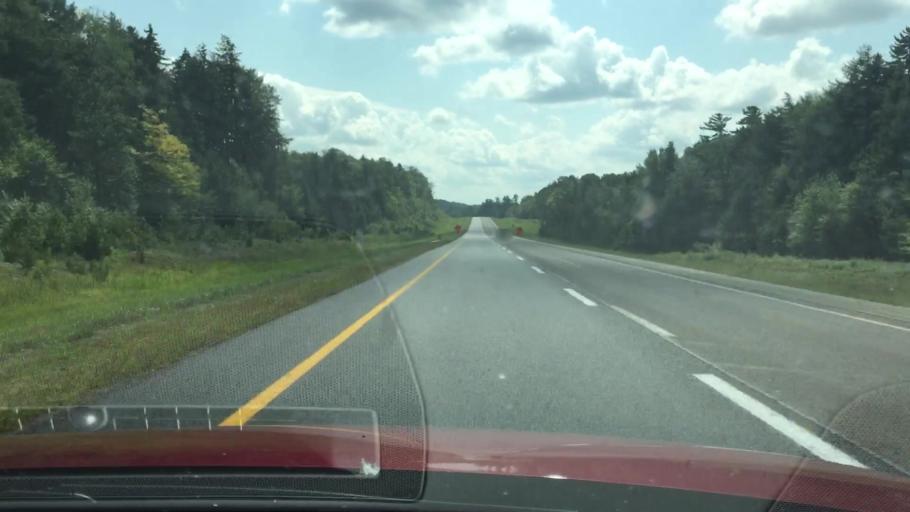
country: US
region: Maine
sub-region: Penobscot County
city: Medway
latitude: 45.7266
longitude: -68.4736
